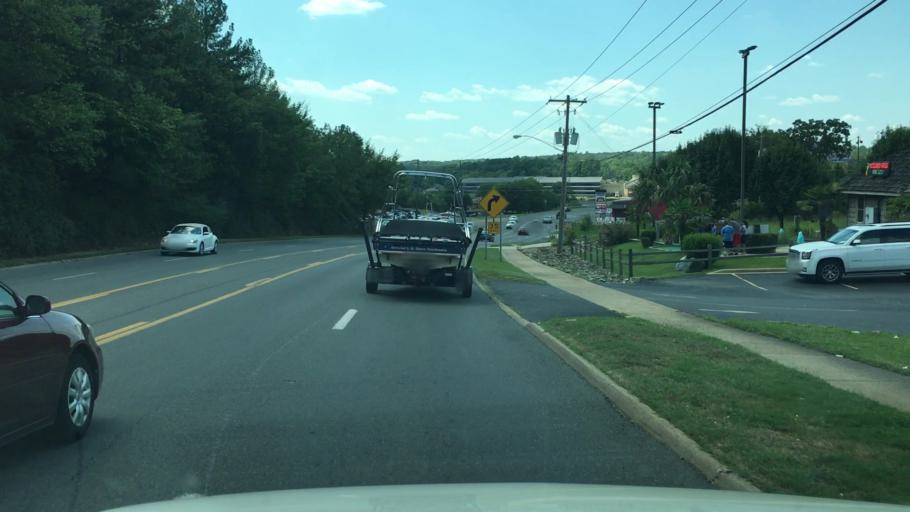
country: US
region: Arkansas
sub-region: Garland County
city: Piney
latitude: 34.4945
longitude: -93.1184
